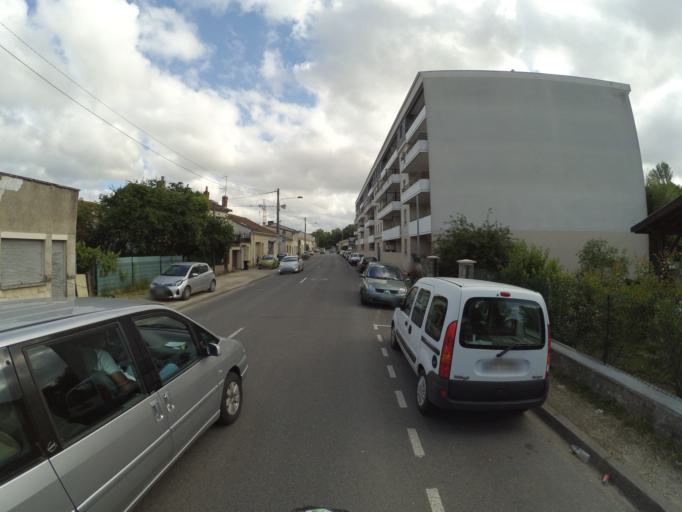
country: FR
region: Aquitaine
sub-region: Departement de la Gironde
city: Lormont
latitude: 44.8781
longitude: -0.5527
